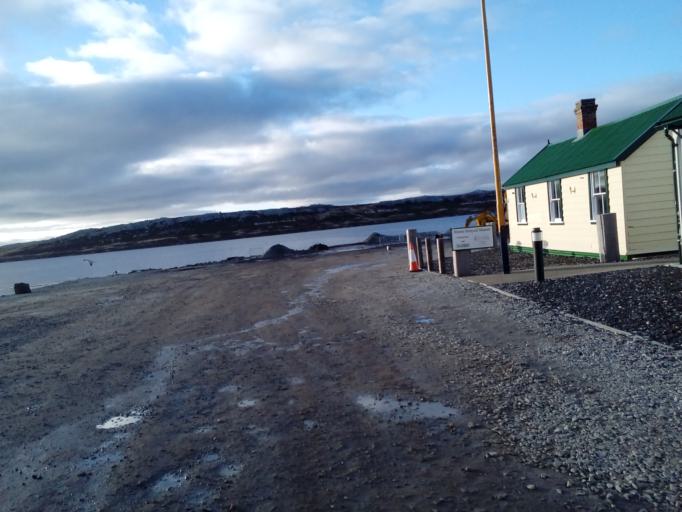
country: FK
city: Stanley
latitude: -51.6911
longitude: -57.8655
